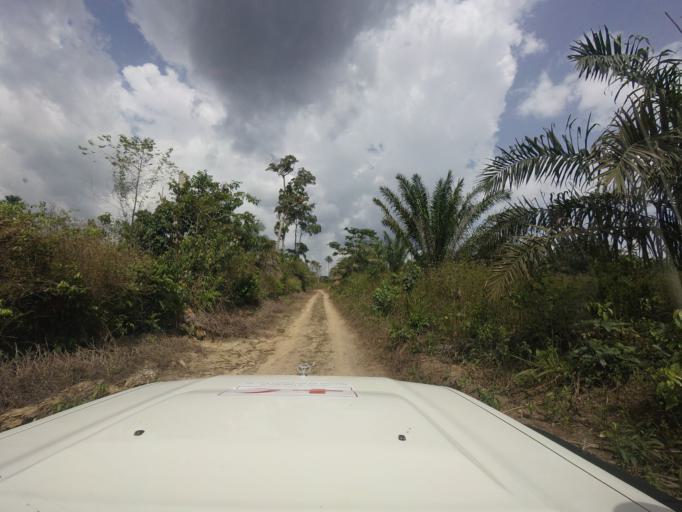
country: LR
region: Lofa
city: Voinjama
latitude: 8.3920
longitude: -9.6099
